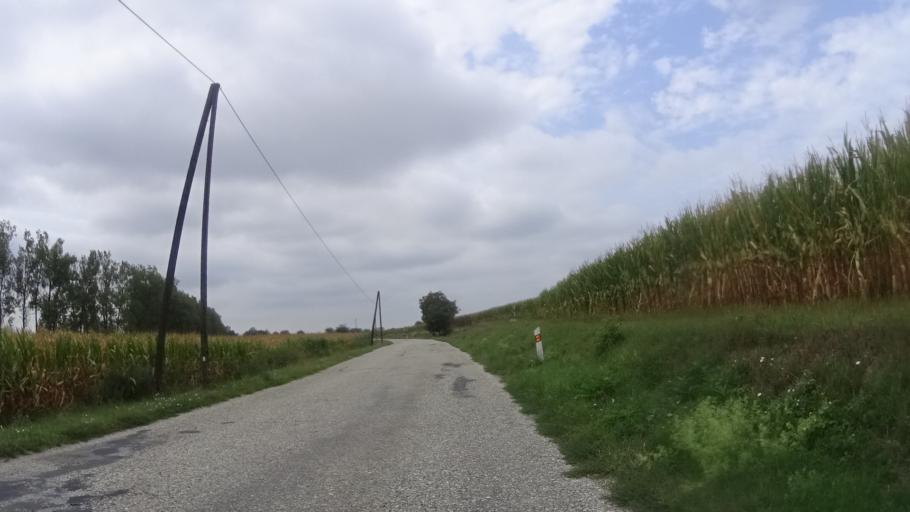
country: HU
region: Komarom-Esztergom
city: Acs
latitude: 47.7695
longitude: 17.9590
